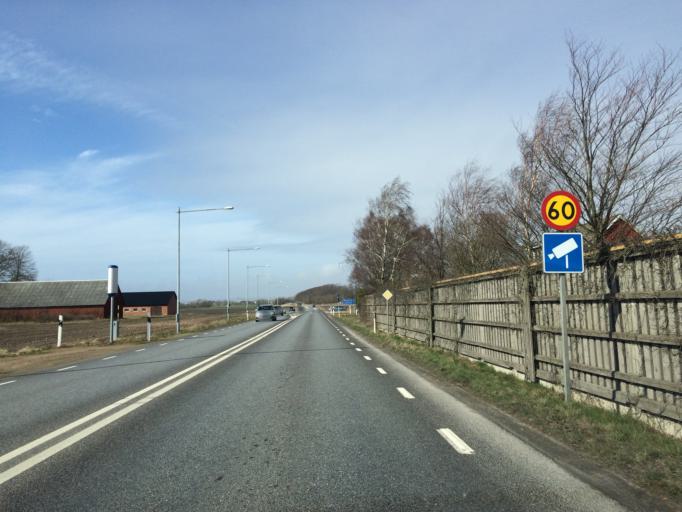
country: SE
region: Halland
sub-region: Halmstads Kommun
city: Paarp
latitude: 56.5962
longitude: 12.9748
